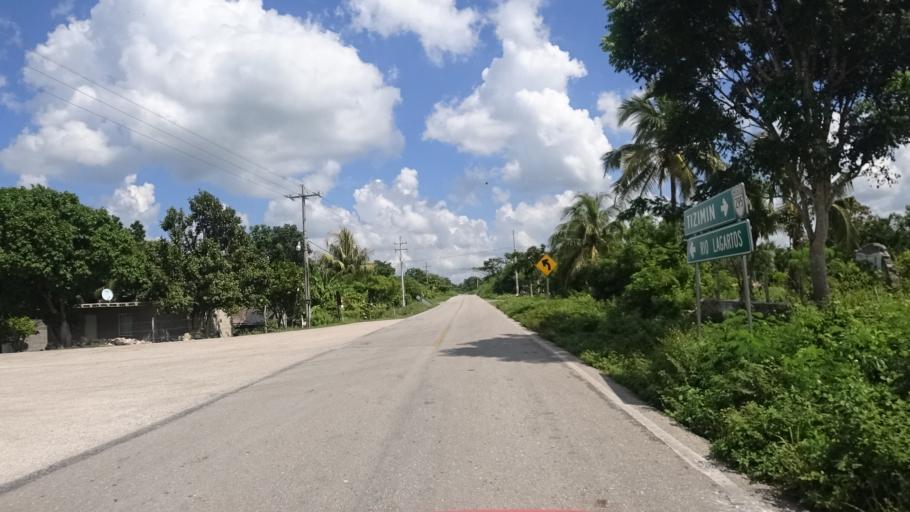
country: MX
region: Yucatan
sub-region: Panaba
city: Loche
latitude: 21.3871
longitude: -88.1421
